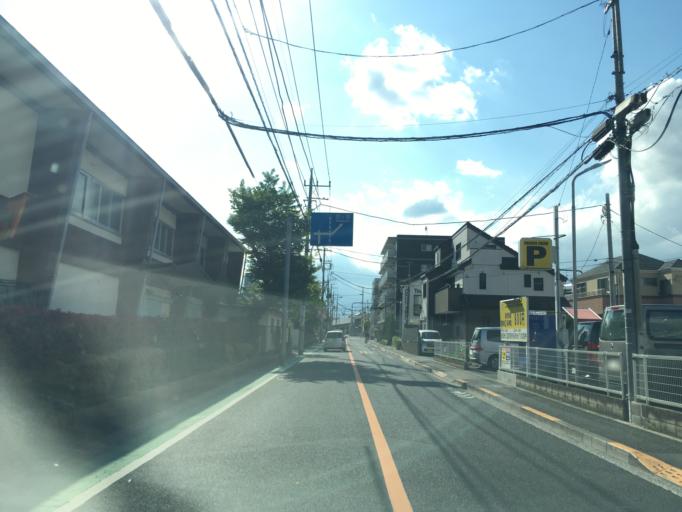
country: JP
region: Tokyo
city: Kokubunji
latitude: 35.7001
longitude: 139.4947
